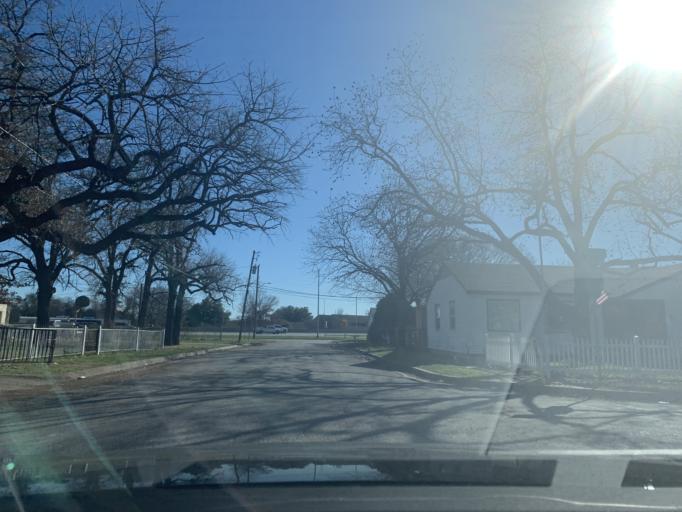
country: US
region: Texas
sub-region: Tarrant County
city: Haltom City
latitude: 32.7775
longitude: -97.2850
